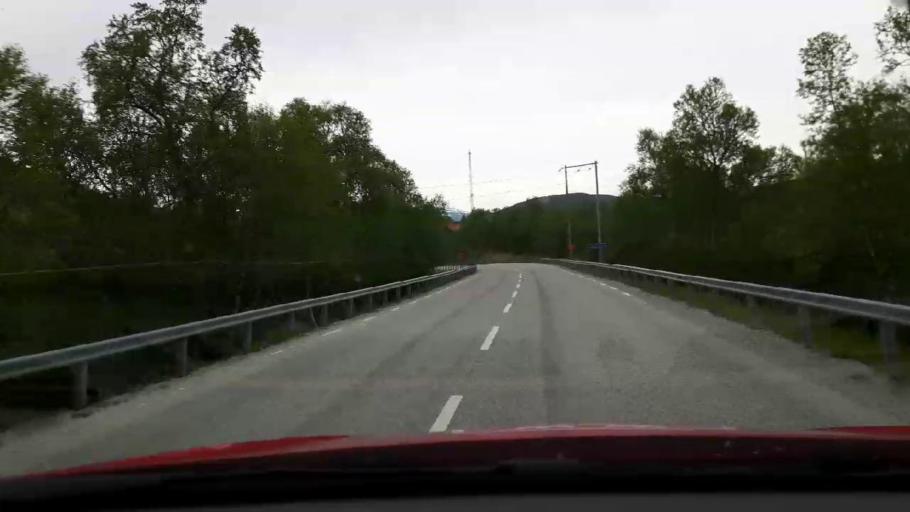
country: NO
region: Sor-Trondelag
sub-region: Tydal
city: Aas
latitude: 62.6992
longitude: 12.3945
